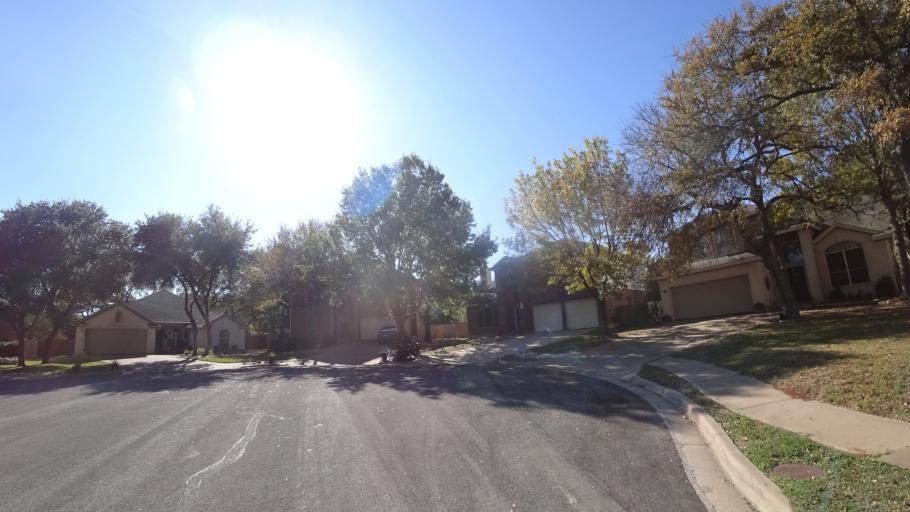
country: US
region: Texas
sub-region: Travis County
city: Barton Creek
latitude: 30.2263
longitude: -97.8668
